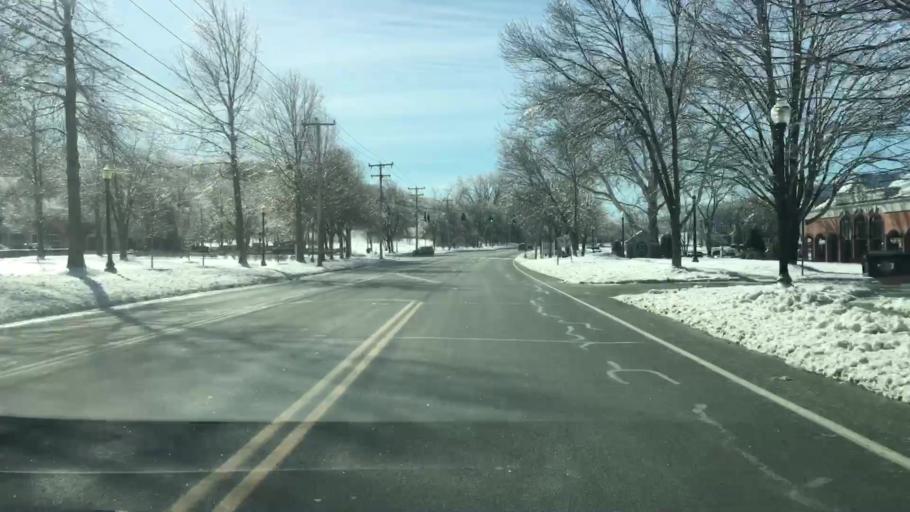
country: US
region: Connecticut
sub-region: New Haven County
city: Heritage Village
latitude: 41.4632
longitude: -73.2321
